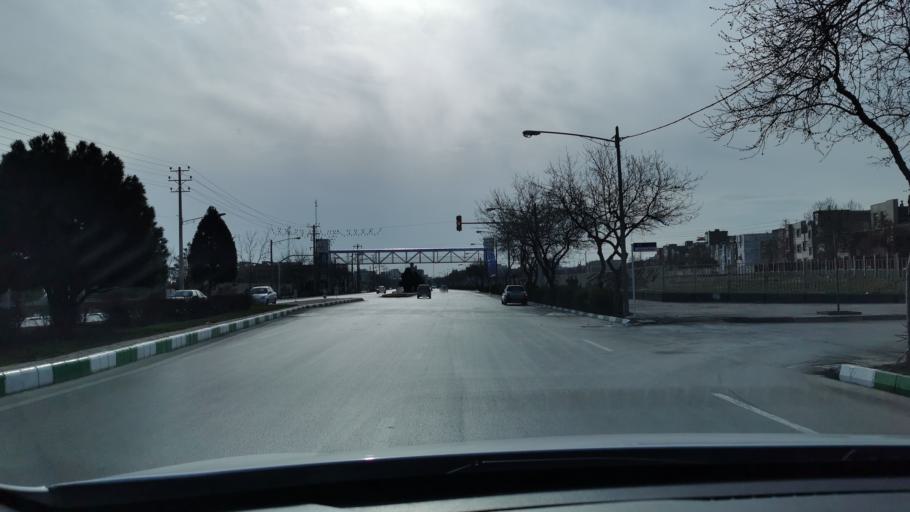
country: IR
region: Razavi Khorasan
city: Mashhad
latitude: 36.3019
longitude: 59.5182
